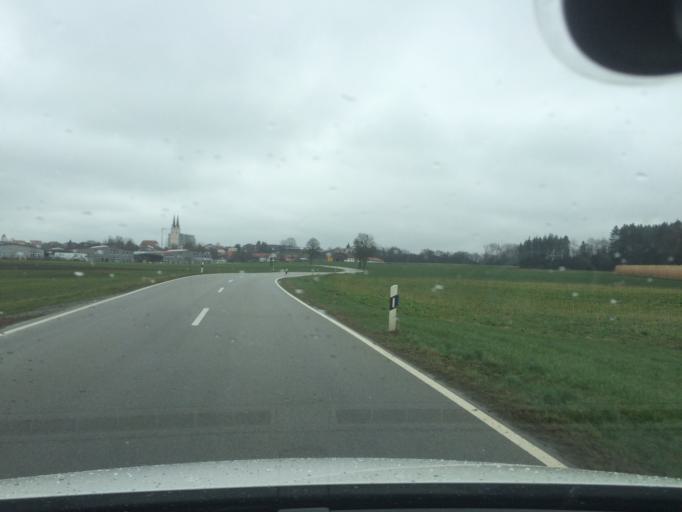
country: DE
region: Bavaria
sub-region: Upper Bavaria
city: Tuntenhausen
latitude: 47.9296
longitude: 12.0066
